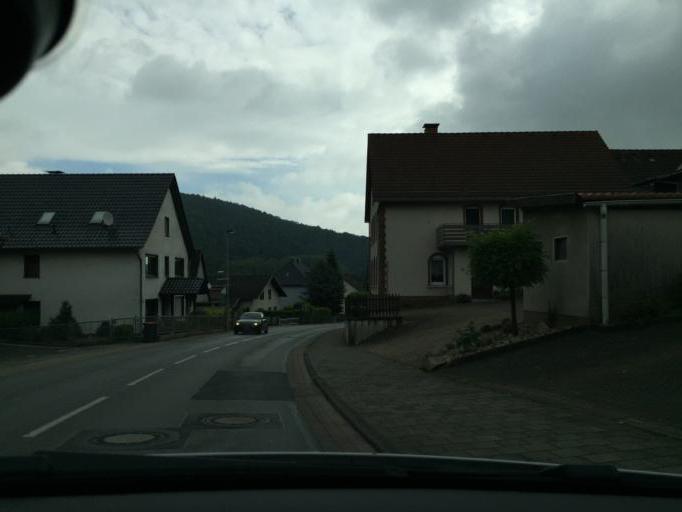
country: DE
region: Lower Saxony
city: Bad Pyrmont
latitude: 51.9894
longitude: 9.3164
